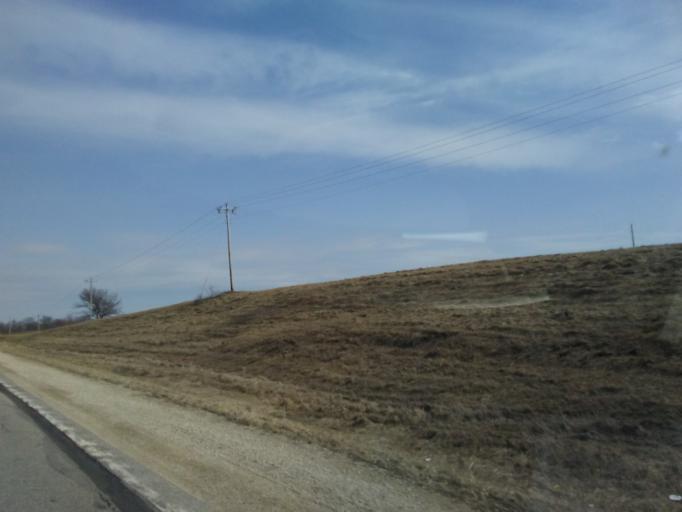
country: US
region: Iowa
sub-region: Winneshiek County
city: Decorah
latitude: 43.2409
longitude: -91.6682
